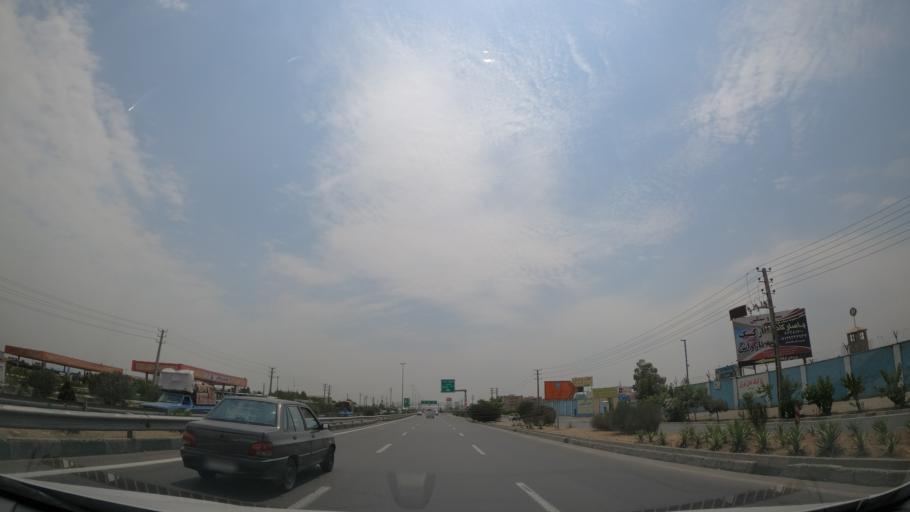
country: IR
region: Tehran
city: Shahr-e Qods
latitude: 35.6982
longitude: 51.1963
